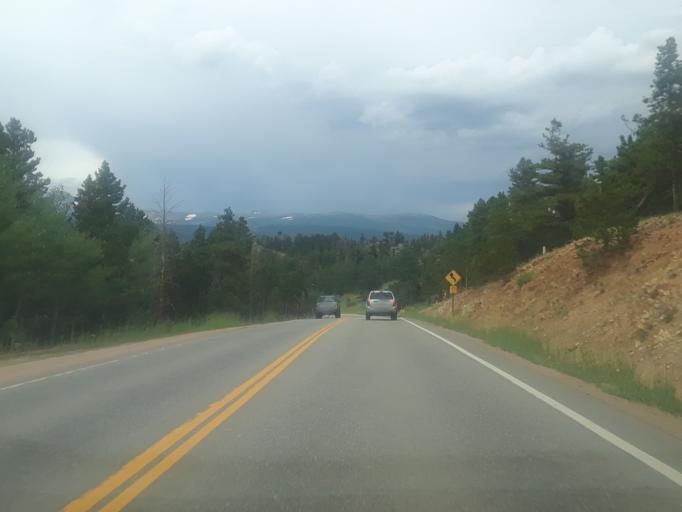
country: US
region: Colorado
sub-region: Boulder County
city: Nederland
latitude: 39.9510
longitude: -105.5045
